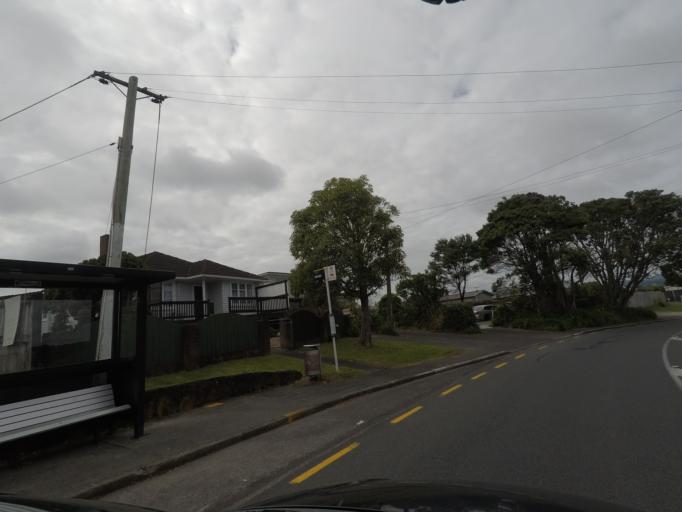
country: NZ
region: Auckland
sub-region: Auckland
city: Rosebank
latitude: -36.8459
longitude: 174.6082
